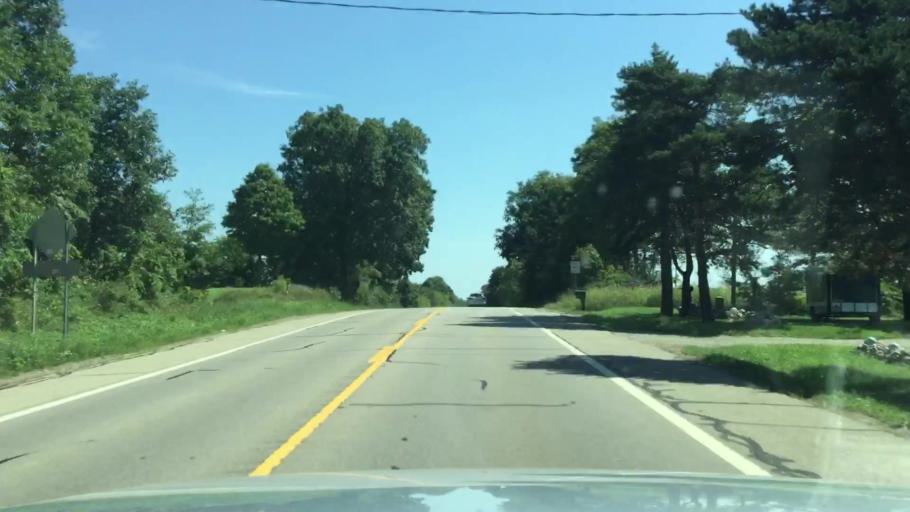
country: US
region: Michigan
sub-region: Lenawee County
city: Clinton
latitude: 42.0730
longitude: -84.0442
